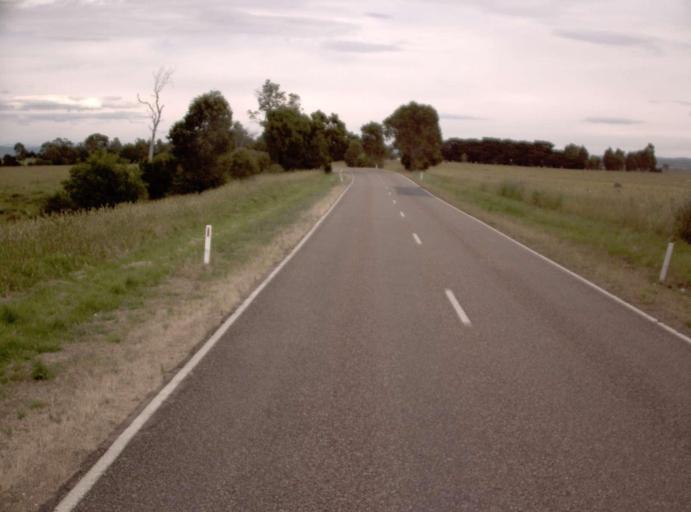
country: AU
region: Victoria
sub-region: East Gippsland
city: Bairnsdale
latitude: -37.8235
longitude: 147.5057
